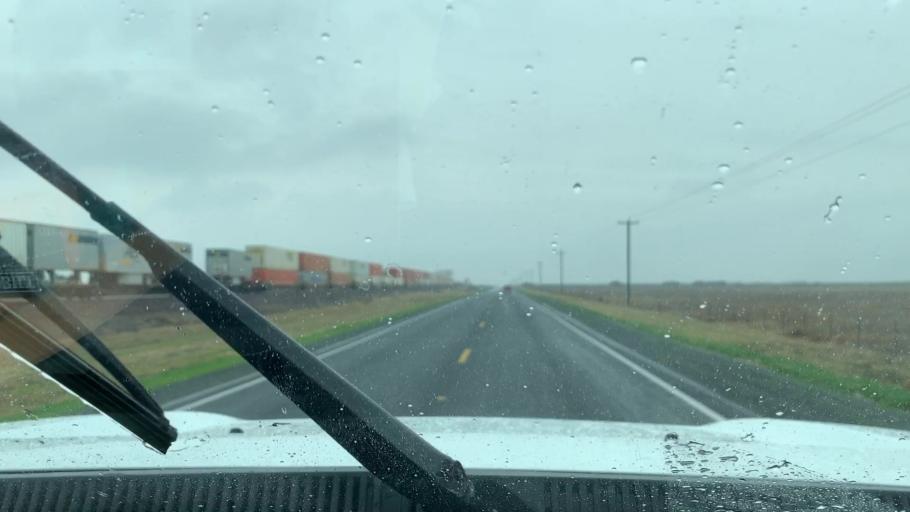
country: US
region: California
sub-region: Tulare County
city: Alpaugh
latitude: 35.9157
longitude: -119.4230
